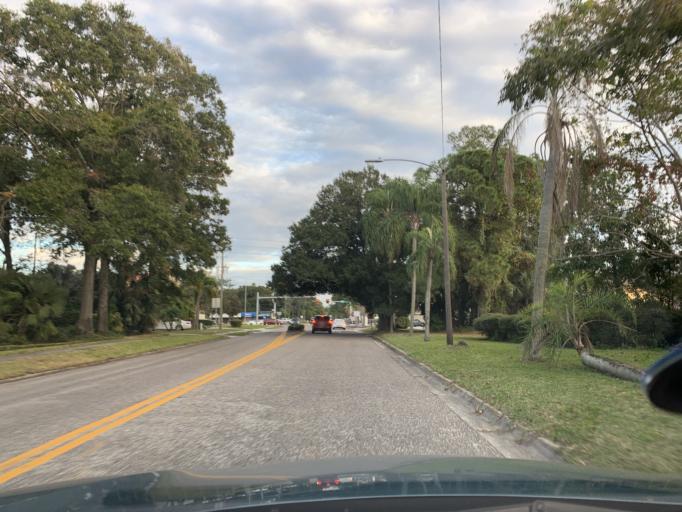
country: US
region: Florida
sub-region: Pinellas County
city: South Pasadena
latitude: 27.7630
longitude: -82.7362
